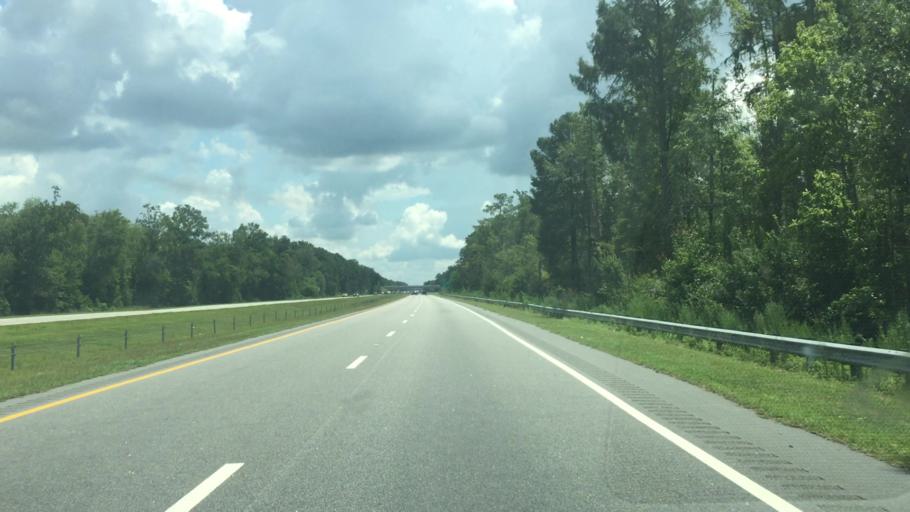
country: US
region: North Carolina
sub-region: Columbus County
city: Chadbourn
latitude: 34.4007
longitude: -78.9126
